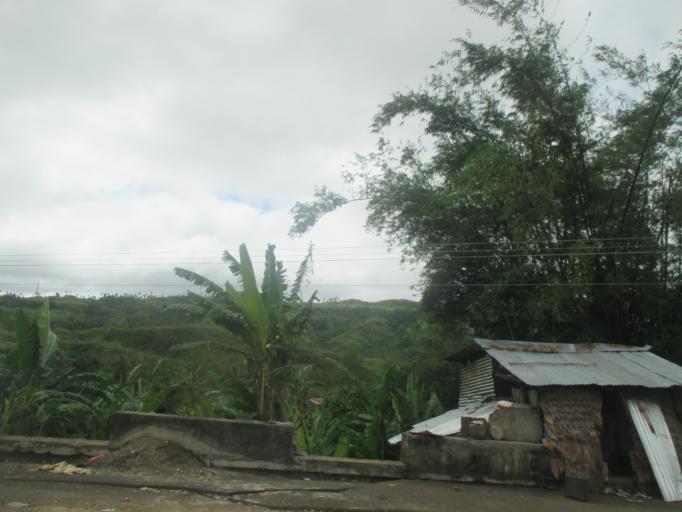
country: PH
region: Eastern Visayas
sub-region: Province of Samar
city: Calbiga
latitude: 11.5577
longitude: 125.0148
